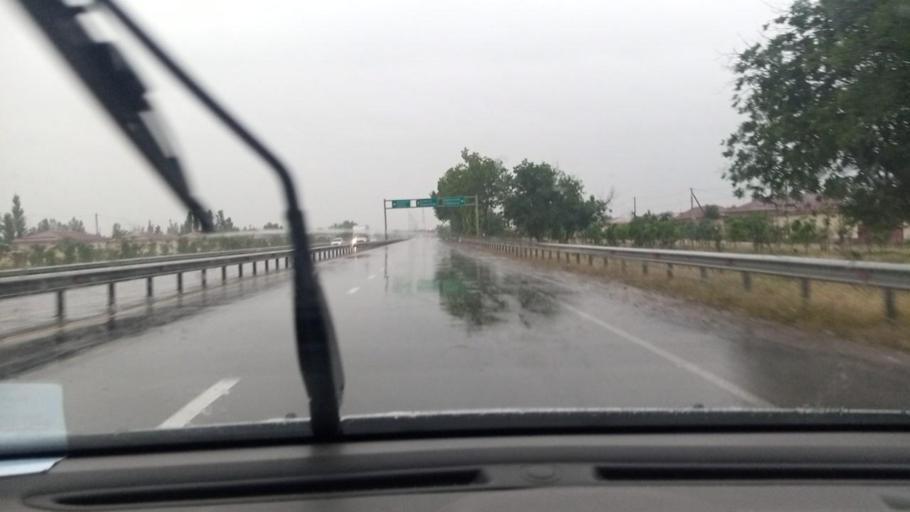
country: UZ
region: Toshkent Shahri
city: Bektemir
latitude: 41.1362
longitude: 69.4345
